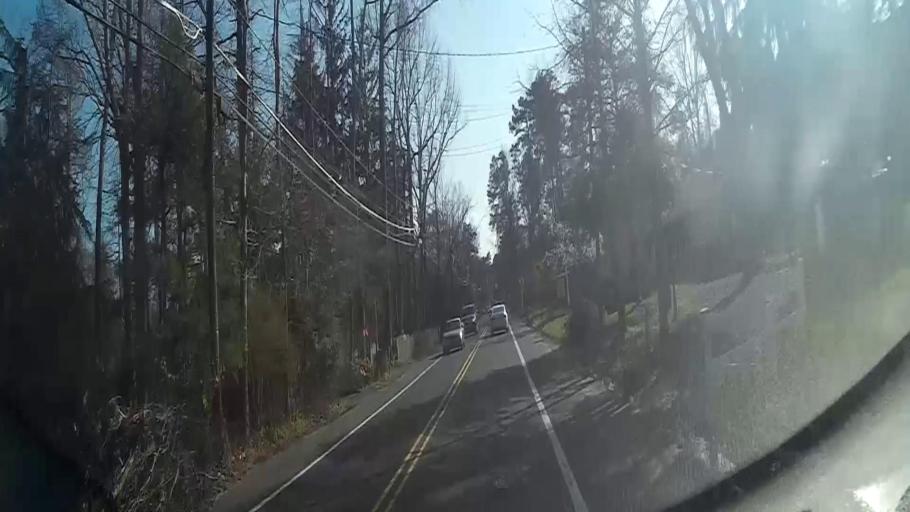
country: US
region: New Jersey
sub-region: Burlington County
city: Medford Lakes
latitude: 39.8648
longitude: -74.8505
